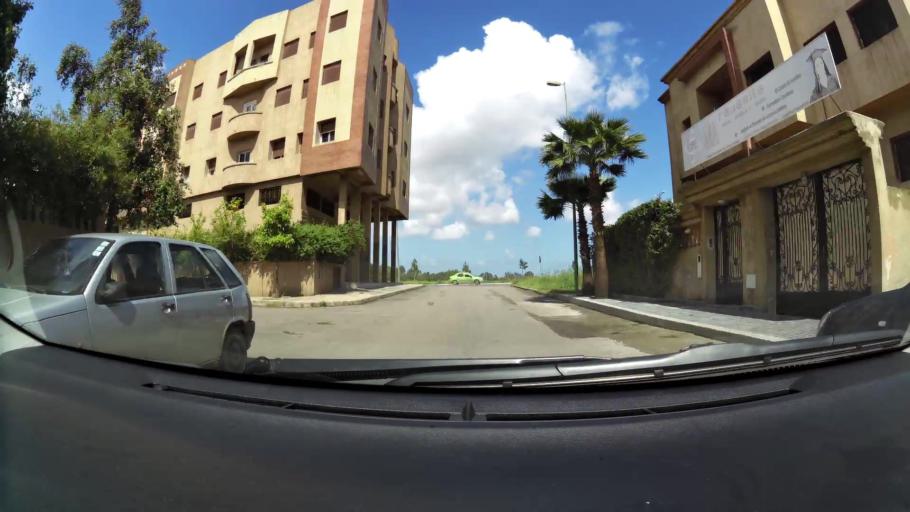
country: MA
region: Grand Casablanca
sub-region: Mediouna
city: Tit Mellil
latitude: 33.5555
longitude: -7.4846
